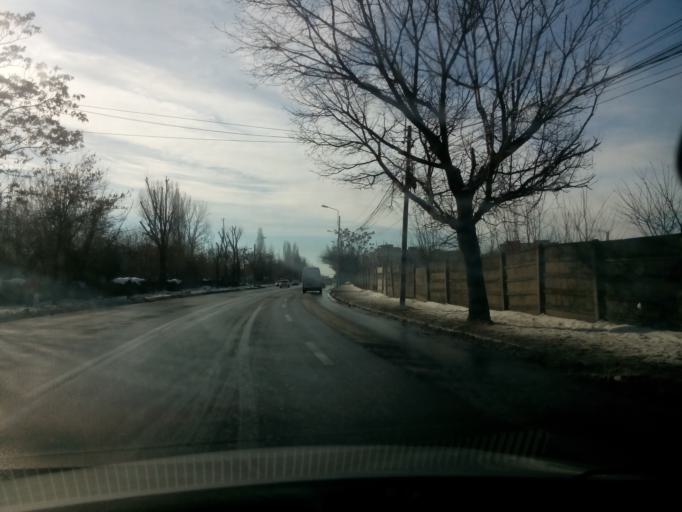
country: RO
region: Ilfov
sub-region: Comuna Popesti-Leordeni
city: Popesti-Leordeni
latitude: 44.3901
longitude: 26.1424
